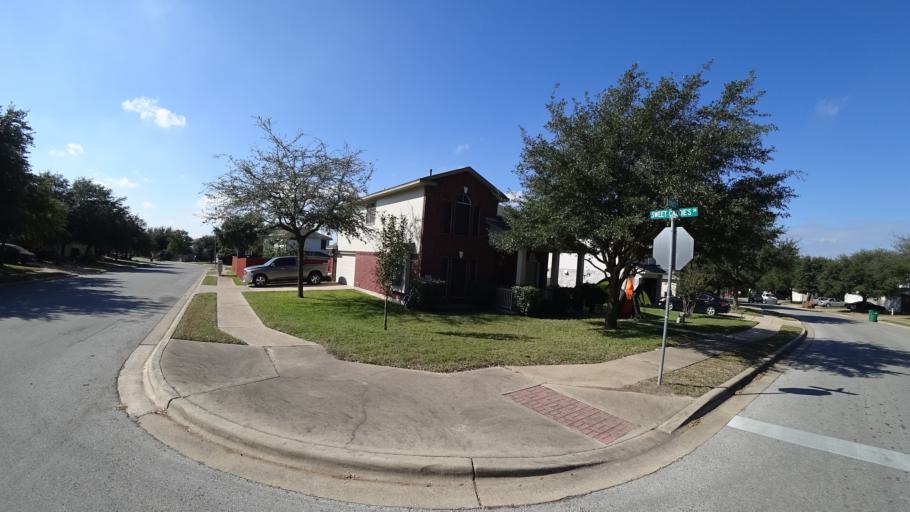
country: US
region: Texas
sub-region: Travis County
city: Windemere
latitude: 30.4425
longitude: -97.6558
